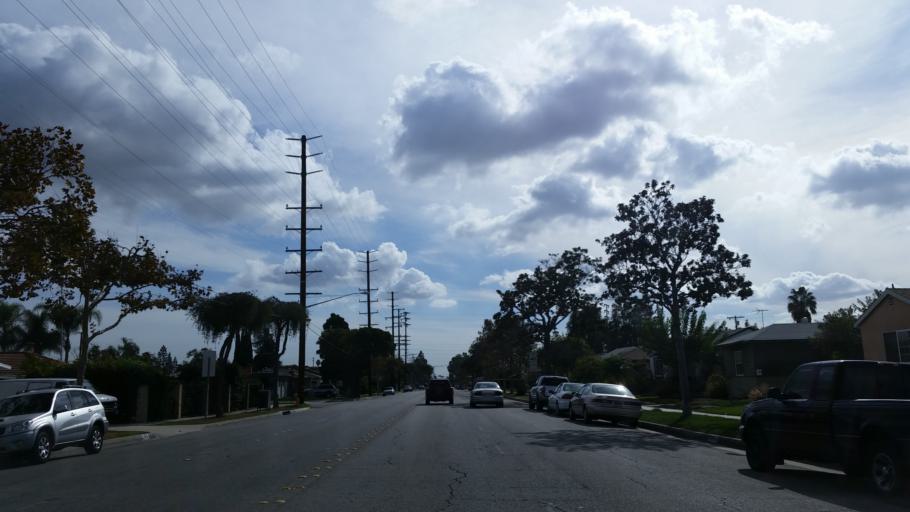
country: US
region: California
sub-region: Los Angeles County
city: Downey
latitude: 33.9088
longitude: -118.1342
